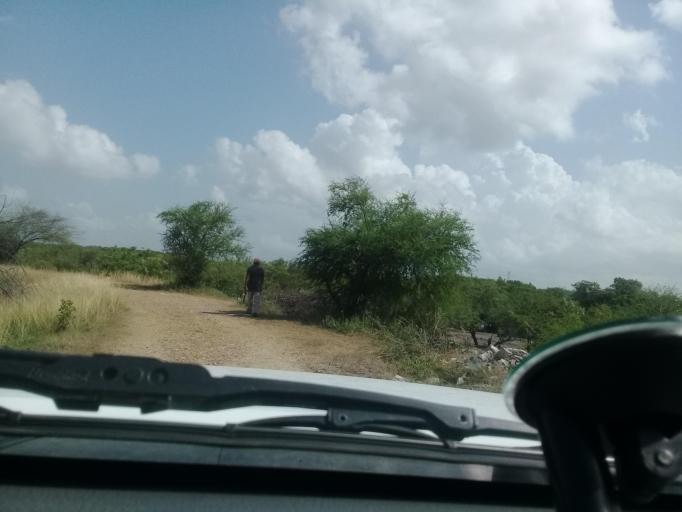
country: MX
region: Veracruz
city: Moralillo
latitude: 22.2288
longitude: -97.8993
